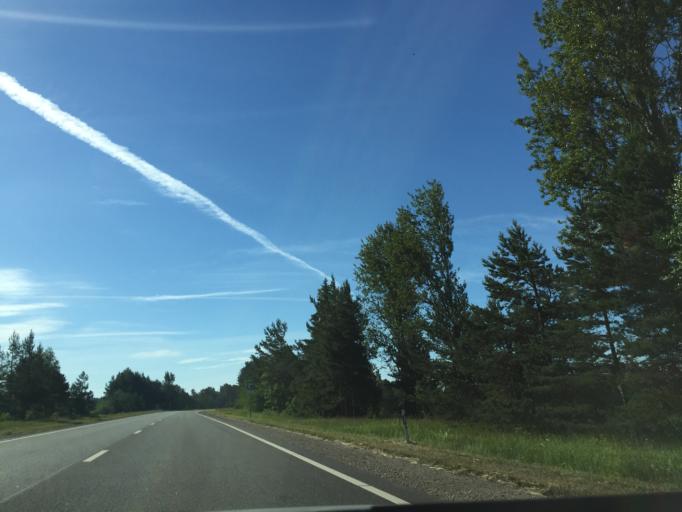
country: LV
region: Ventspils
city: Ventspils
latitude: 57.4004
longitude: 21.6886
